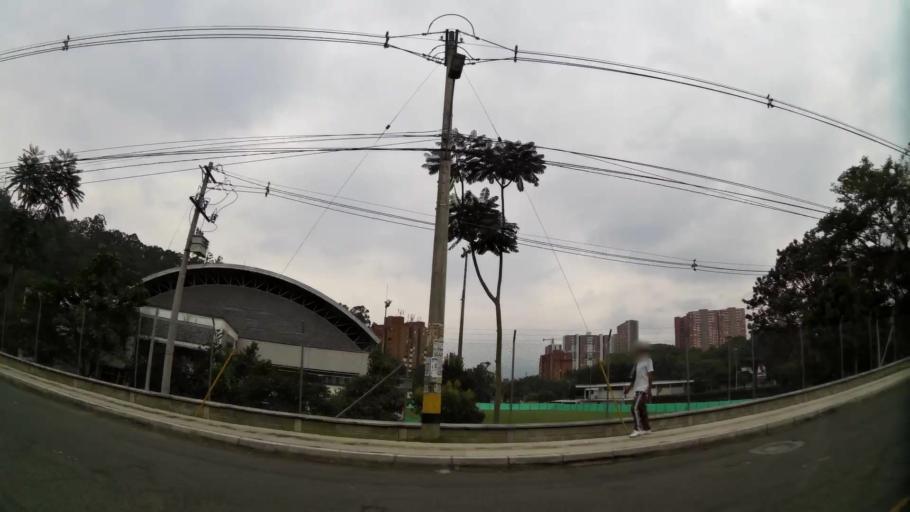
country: CO
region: Antioquia
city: Medellin
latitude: 6.2726
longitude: -75.5865
